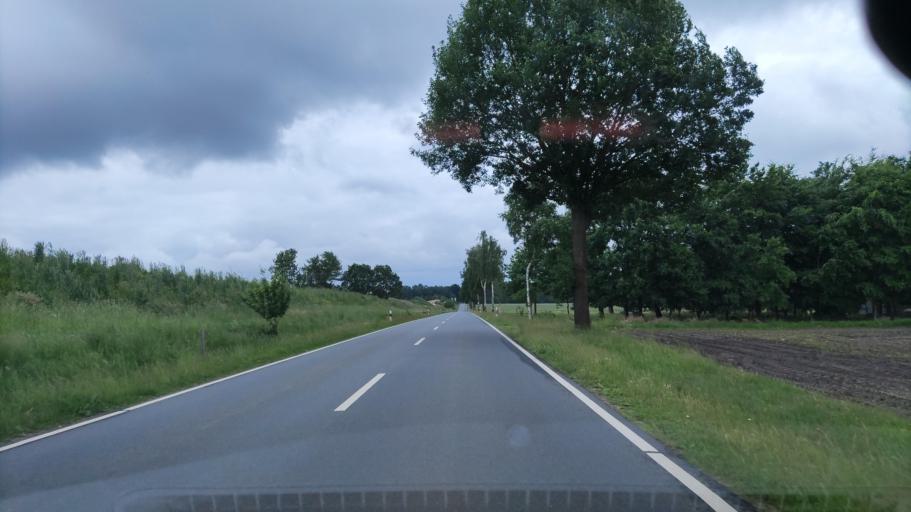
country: DE
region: Lower Saxony
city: Neuenkirchen
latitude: 53.0963
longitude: 9.6722
